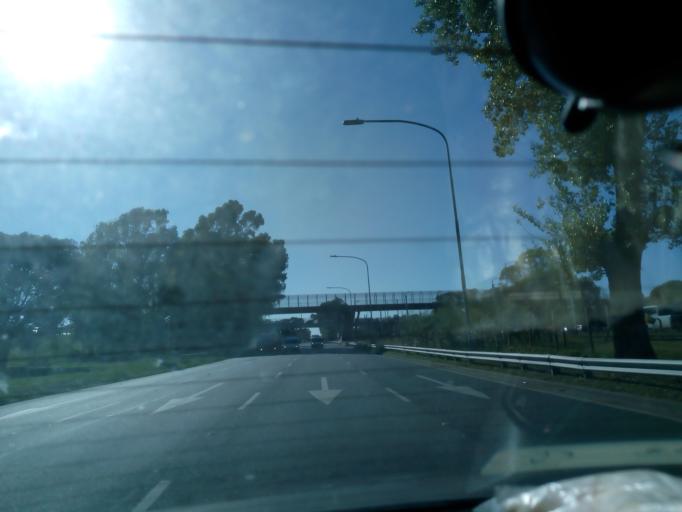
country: AR
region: Buenos Aires F.D.
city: Colegiales
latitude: -34.5474
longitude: -58.4395
